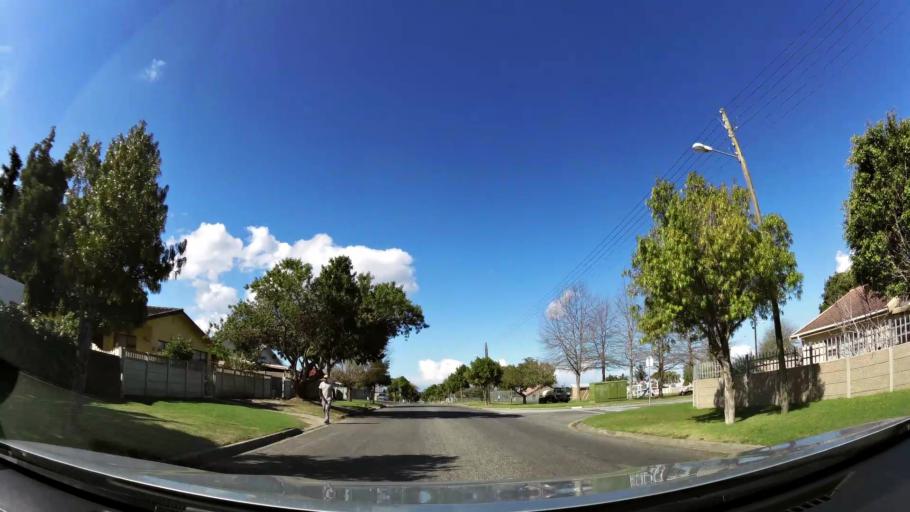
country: ZA
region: Western Cape
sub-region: Eden District Municipality
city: George
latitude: -33.9490
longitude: 22.4741
